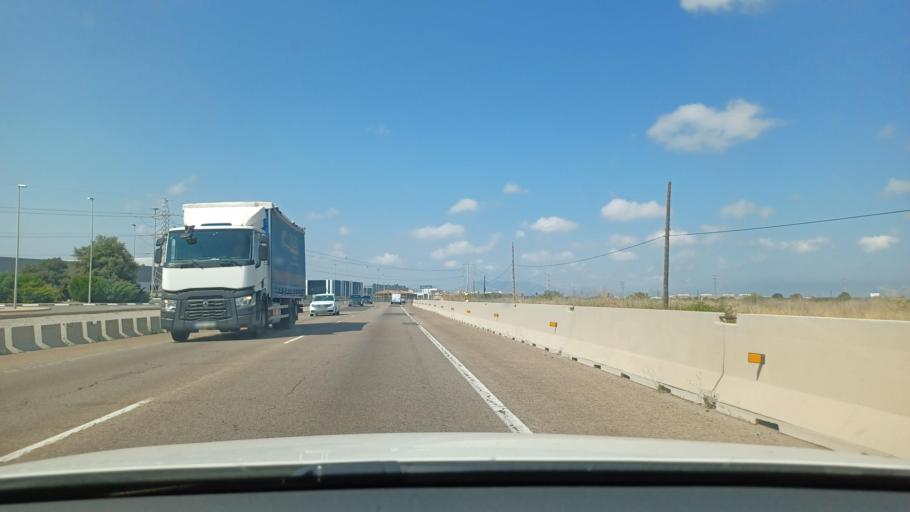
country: ES
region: Valencia
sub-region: Provincia de Castello
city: Vila-real
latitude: 39.9133
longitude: -0.1128
